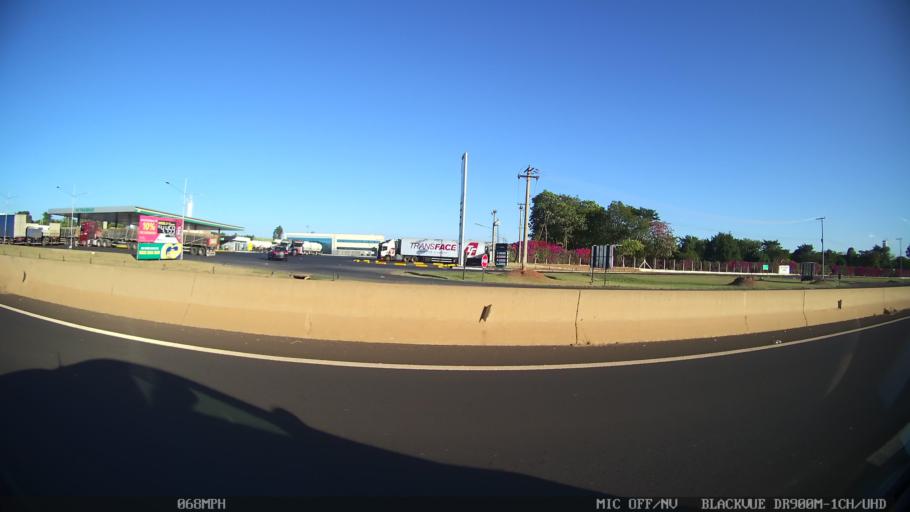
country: BR
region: Sao Paulo
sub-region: Guapiacu
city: Guapiacu
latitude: -20.7901
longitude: -49.2941
